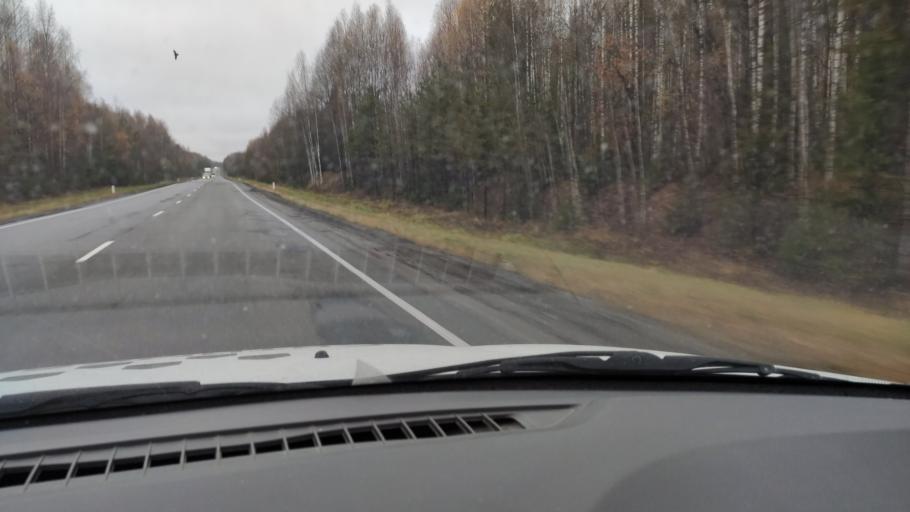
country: RU
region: Kirov
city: Chernaya Kholunitsa
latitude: 58.7706
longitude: 51.9580
